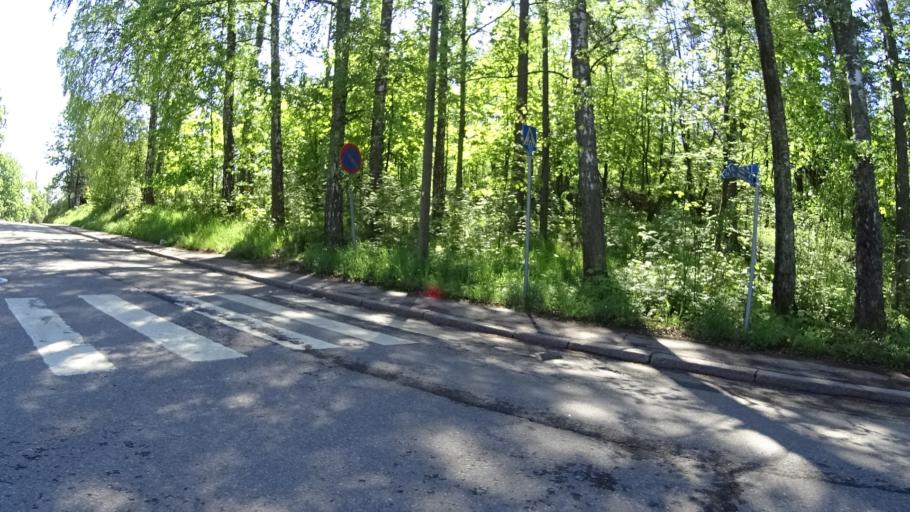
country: FI
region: Uusimaa
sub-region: Helsinki
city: Helsinki
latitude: 60.1643
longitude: 24.8827
